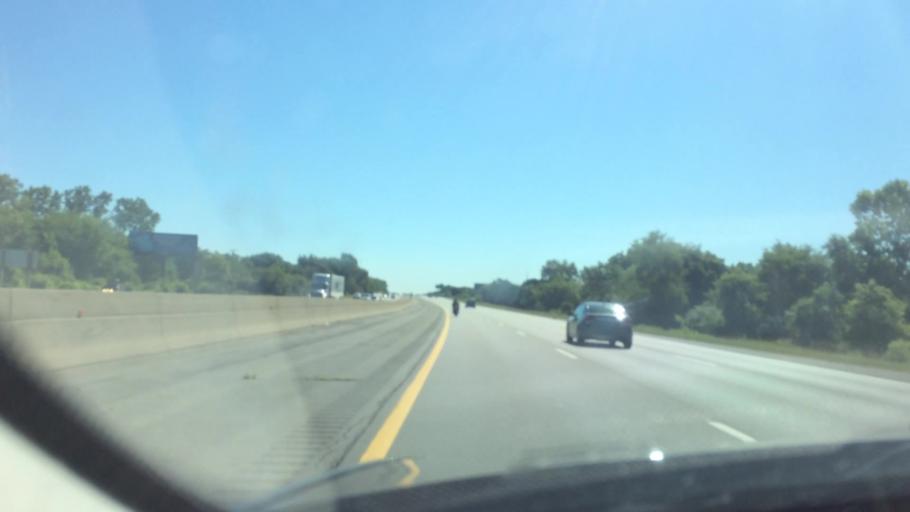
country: US
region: Michigan
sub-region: Washtenaw County
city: Ypsilanti
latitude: 42.2253
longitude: -83.6309
